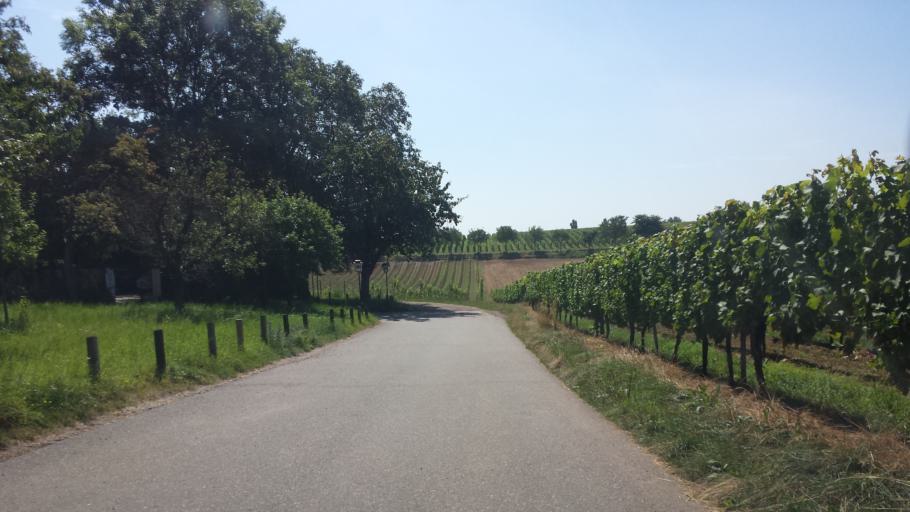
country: DE
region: Rheinland-Pfalz
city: Landau in der Pfalz
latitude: 49.1870
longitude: 8.0947
